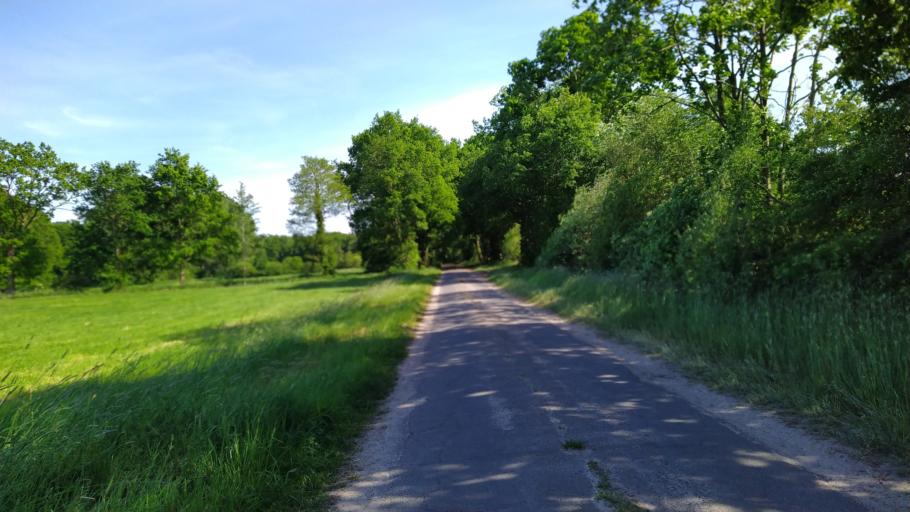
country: DE
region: Lower Saxony
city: Ahlerstedt
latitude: 53.4283
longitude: 9.4711
